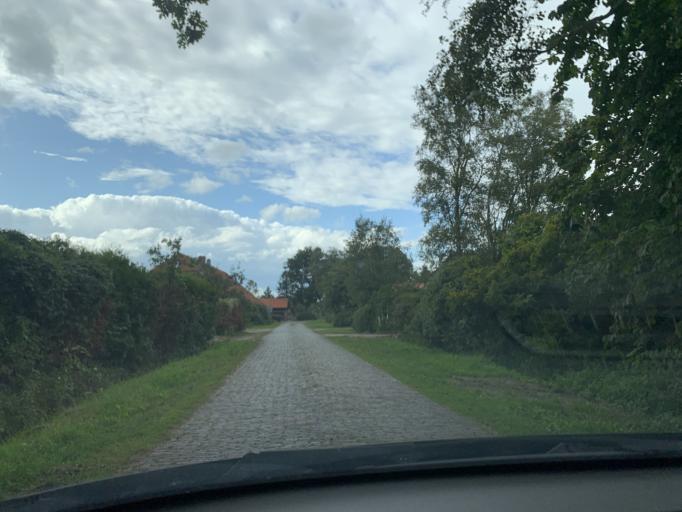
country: DE
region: Lower Saxony
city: Westerstede
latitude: 53.2768
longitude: 7.9779
